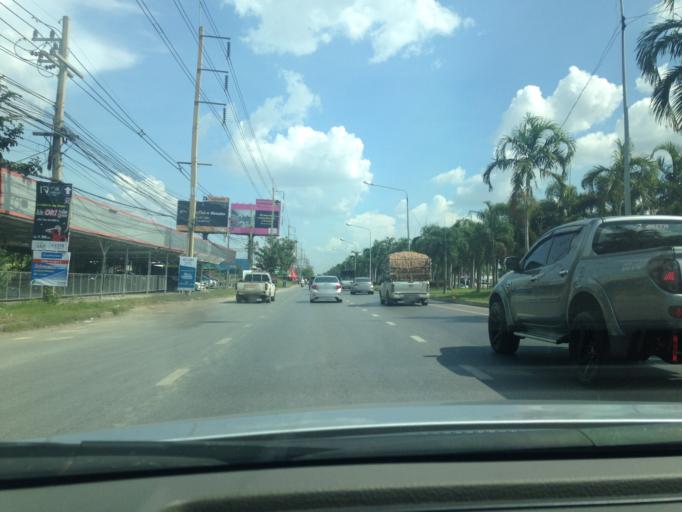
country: TH
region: Phra Nakhon Si Ayutthaya
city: Ban Bang Kadi Pathum Thani
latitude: 13.9990
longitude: 100.5723
